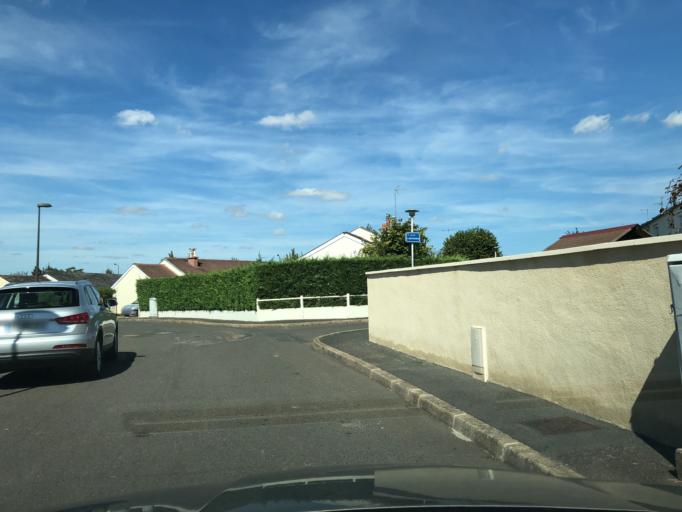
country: FR
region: Centre
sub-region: Departement d'Indre-et-Loire
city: Saint-Cyr-sur-Loire
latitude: 47.4257
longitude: 0.6880
